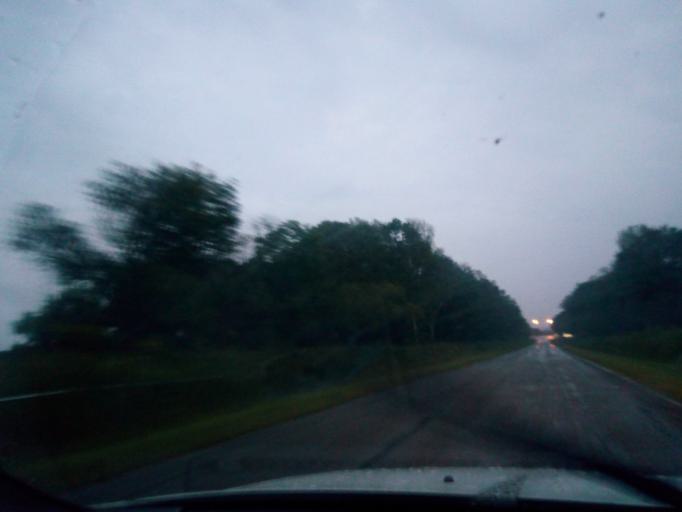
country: RU
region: Primorskiy
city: Dal'nerechensk
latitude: 45.8701
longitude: 133.7163
